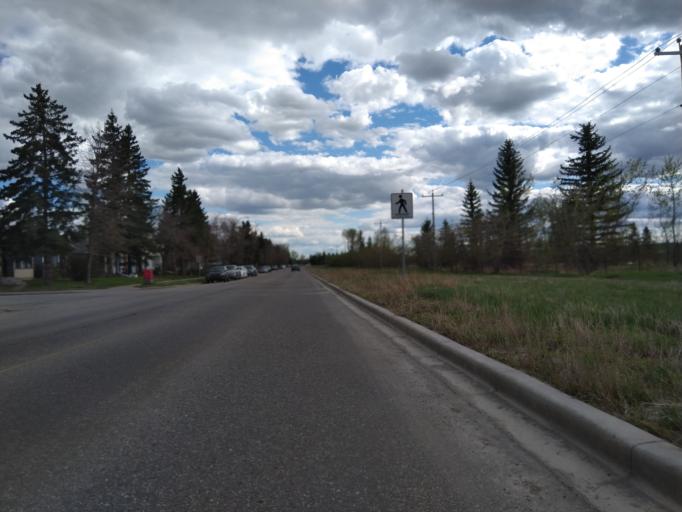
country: CA
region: Alberta
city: Calgary
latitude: 50.9989
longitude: -114.1411
